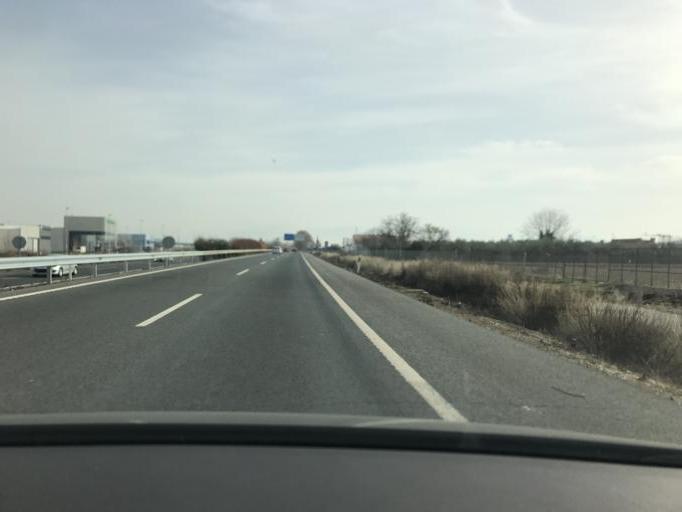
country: ES
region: Andalusia
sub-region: Provincia de Granada
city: Chauchina
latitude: 37.1917
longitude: -3.7858
